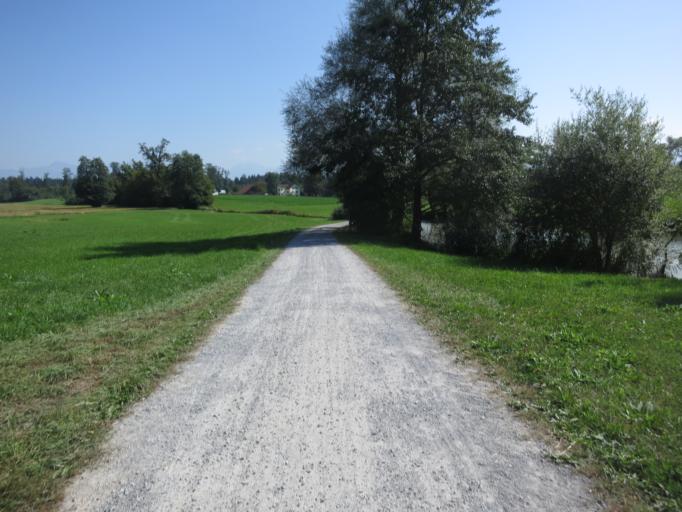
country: CH
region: Zurich
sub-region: Bezirk Hinwil
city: Bubikon
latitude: 47.2622
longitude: 8.8185
